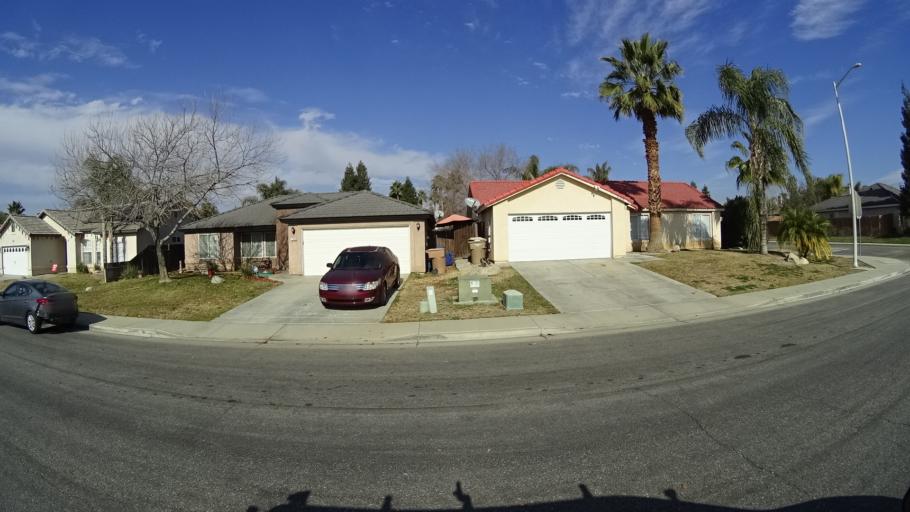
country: US
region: California
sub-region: Kern County
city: Lamont
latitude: 35.3928
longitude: -118.8794
